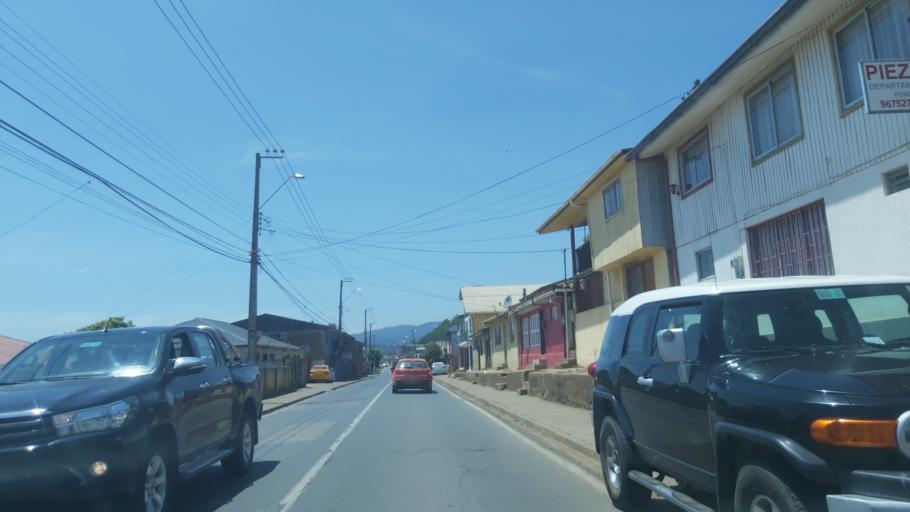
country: CL
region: Maule
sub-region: Provincia de Cauquenes
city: Cauquenes
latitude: -35.8157
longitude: -72.5791
